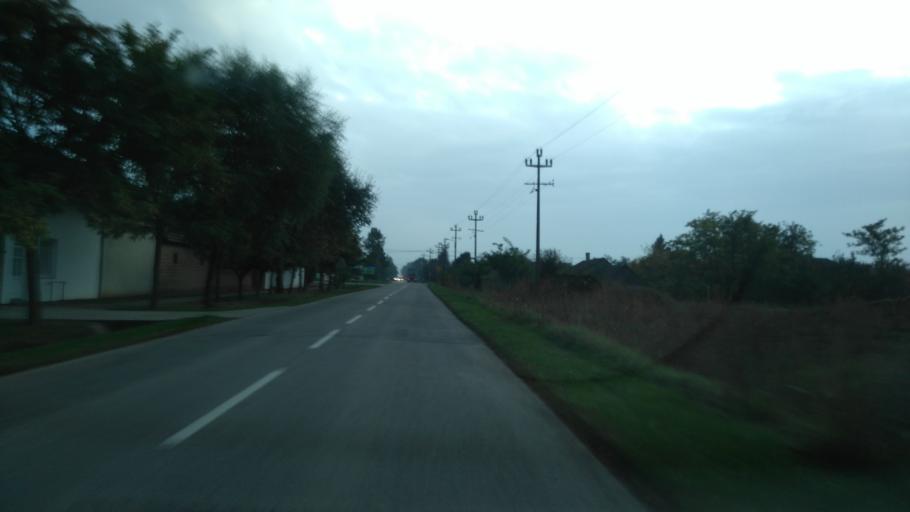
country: RS
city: Mol
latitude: 45.7730
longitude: 20.1285
